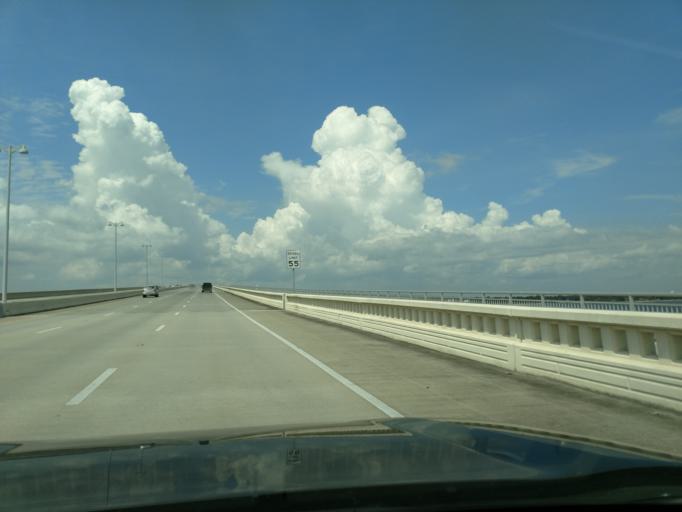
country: US
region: Mississippi
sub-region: Jackson County
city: Ocean Springs
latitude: 30.4014
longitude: -88.8491
